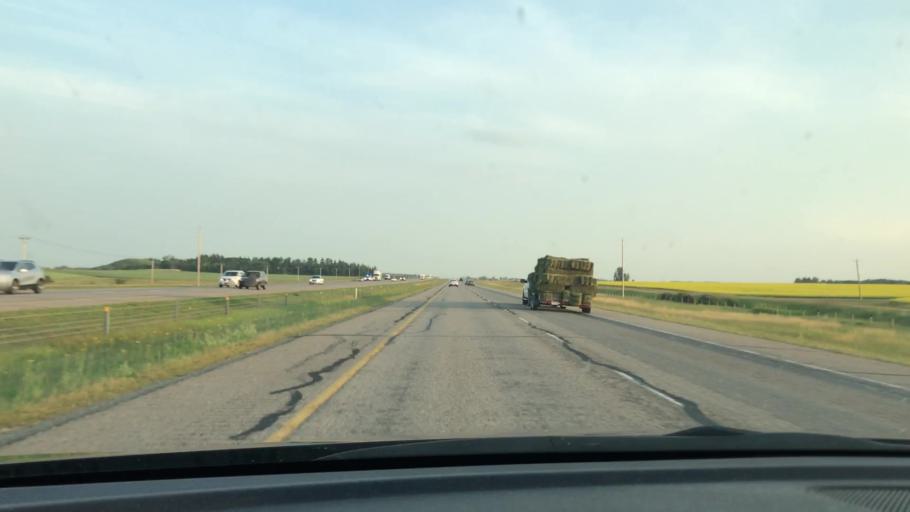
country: CA
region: Alberta
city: Olds
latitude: 51.8660
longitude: -114.0256
